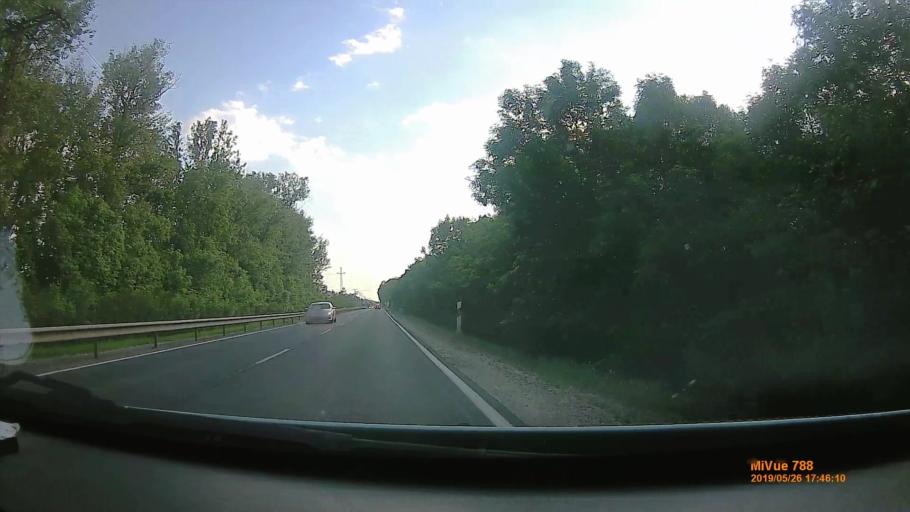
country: HU
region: Borsod-Abauj-Zemplen
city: Szikszo
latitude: 48.2107
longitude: 20.9407
